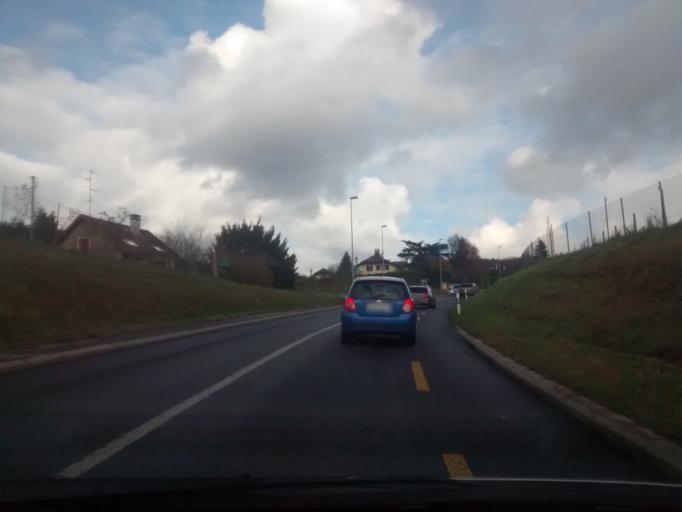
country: CH
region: Vaud
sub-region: Ouest Lausannois District
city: Crissier
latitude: 46.5568
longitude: 6.5734
